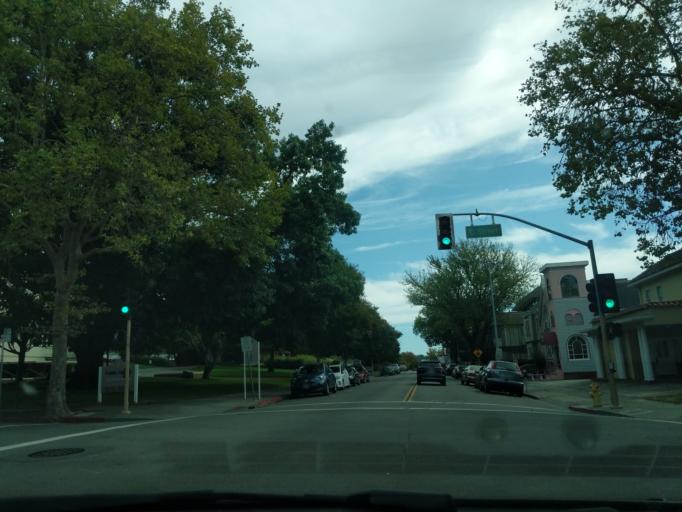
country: US
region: California
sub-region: Marin County
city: San Rafael
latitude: 37.9747
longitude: -122.5333
